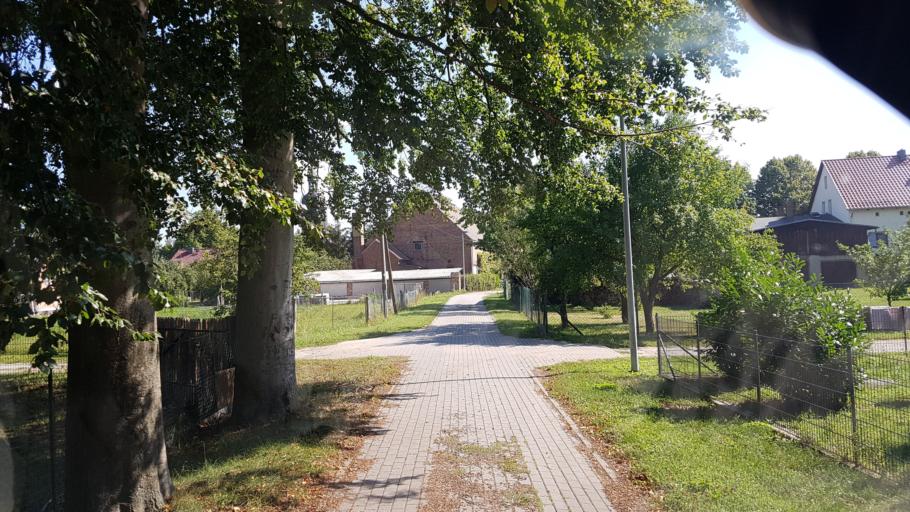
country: DE
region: Brandenburg
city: Vetschau
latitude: 51.7121
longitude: 14.0857
